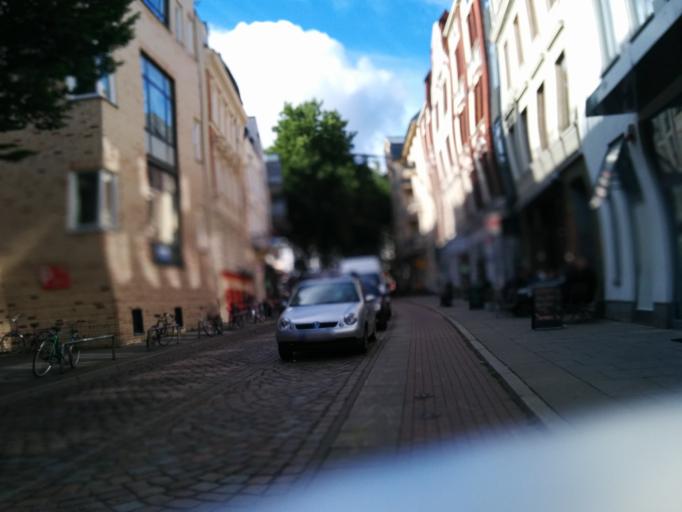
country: DE
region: Hamburg
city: Altona
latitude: 53.5529
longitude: 9.9311
